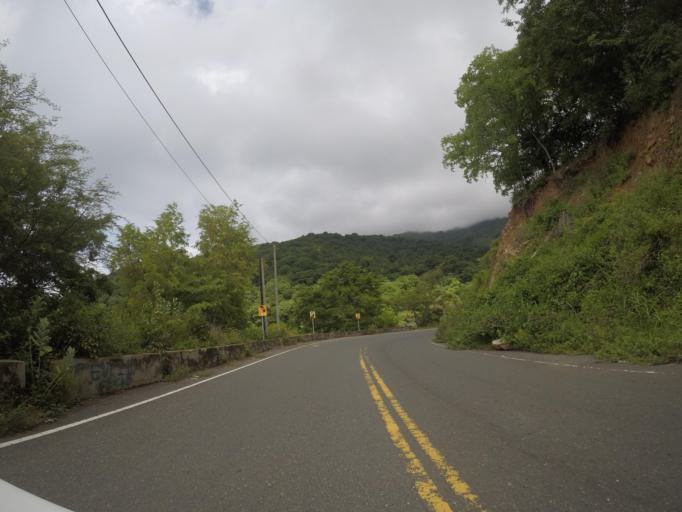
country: TL
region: Liquica
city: Maubara
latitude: -8.6774
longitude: 125.1094
